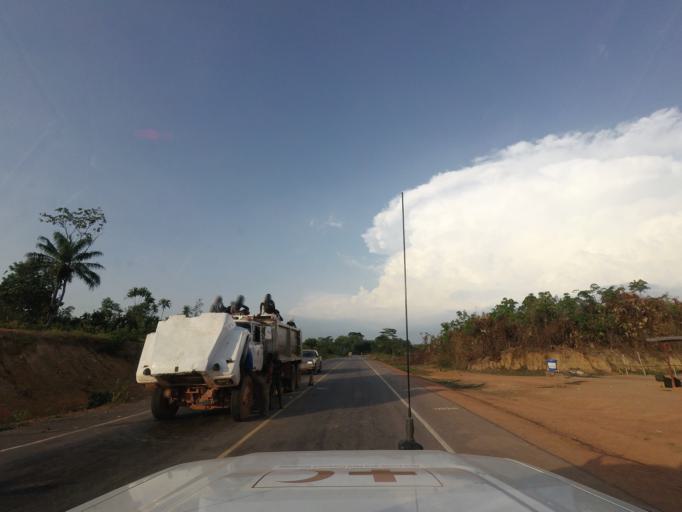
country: LR
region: Bong
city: Gbarnga
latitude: 7.0663
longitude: -9.1580
